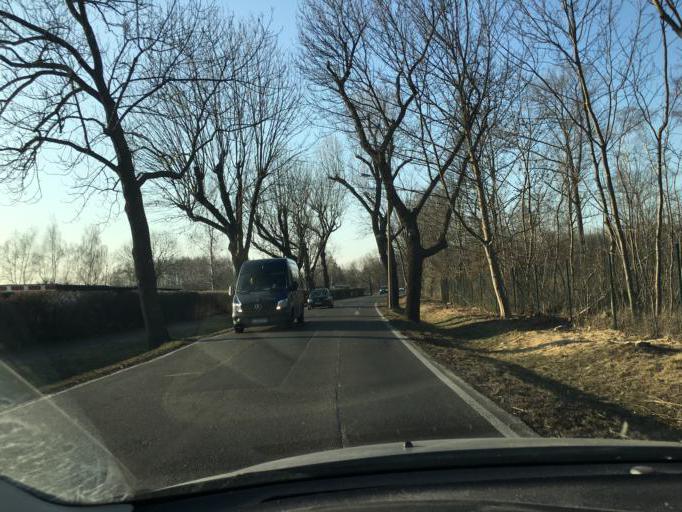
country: DE
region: Saxony
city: Grossposna
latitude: 51.3135
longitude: 12.4419
